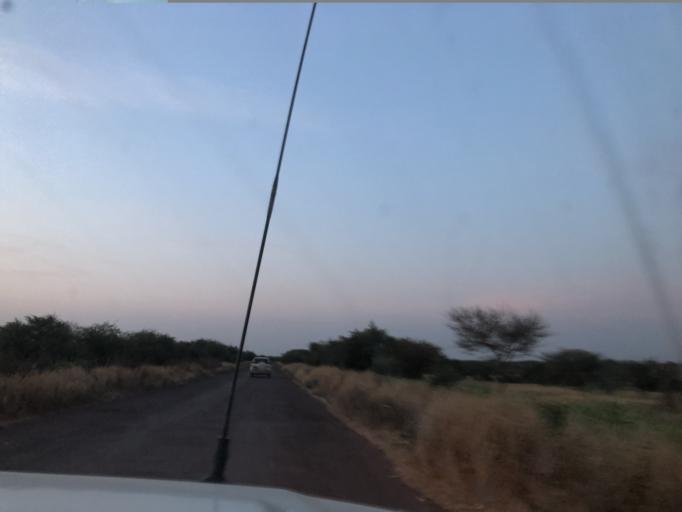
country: TD
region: Mayo-Kebbi Est
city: Guelendeng
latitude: 11.1819
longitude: 15.3628
